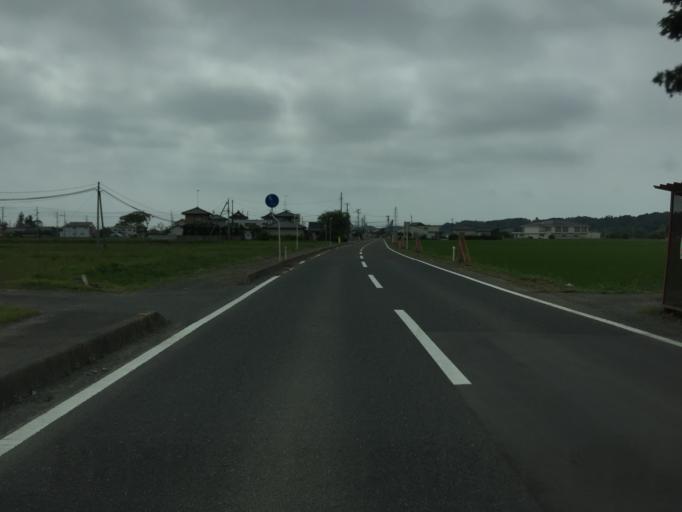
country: JP
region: Fukushima
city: Namie
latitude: 37.6921
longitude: 140.9784
